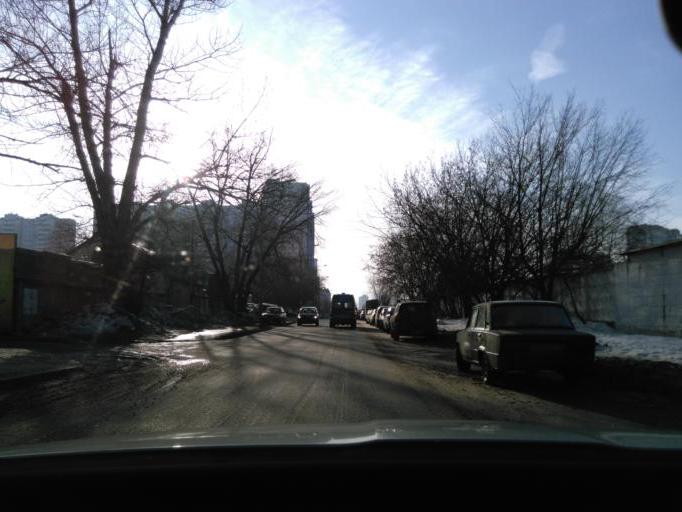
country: RU
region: Moskovskaya
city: Levoberezhnaya
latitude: 55.8735
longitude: 37.4720
